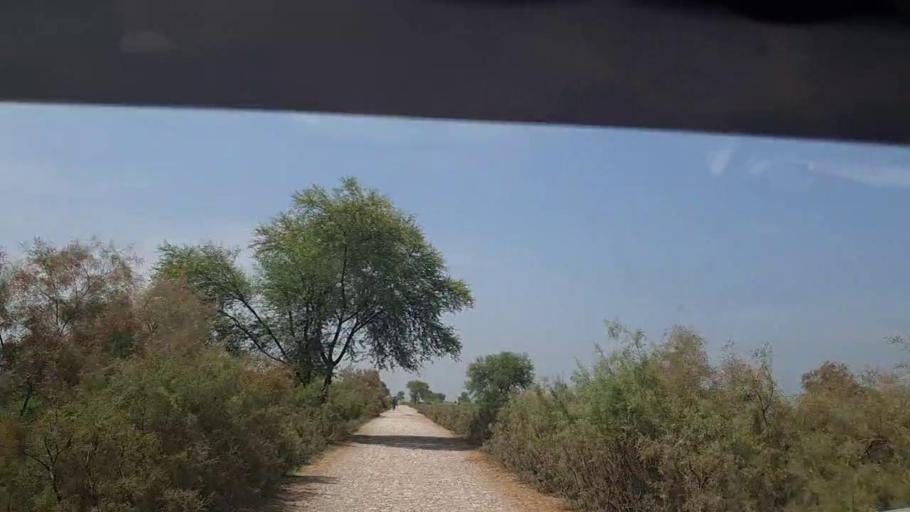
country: PK
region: Sindh
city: Thul
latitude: 28.2076
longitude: 68.6914
